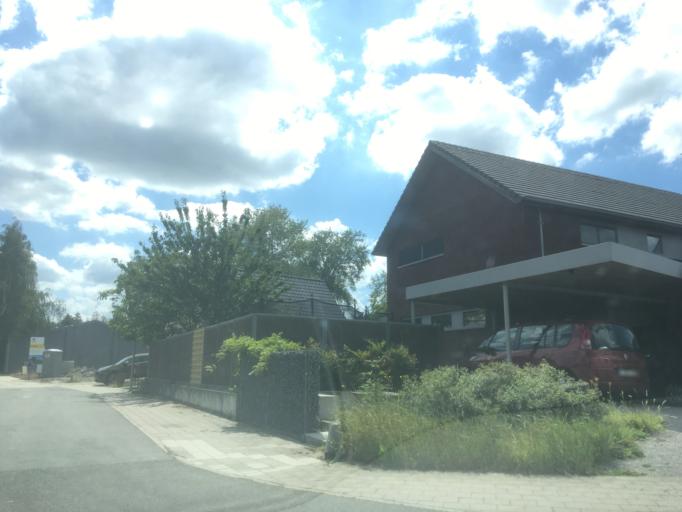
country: BE
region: Flanders
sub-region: Provincie West-Vlaanderen
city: Staden
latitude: 50.9364
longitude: 3.0173
